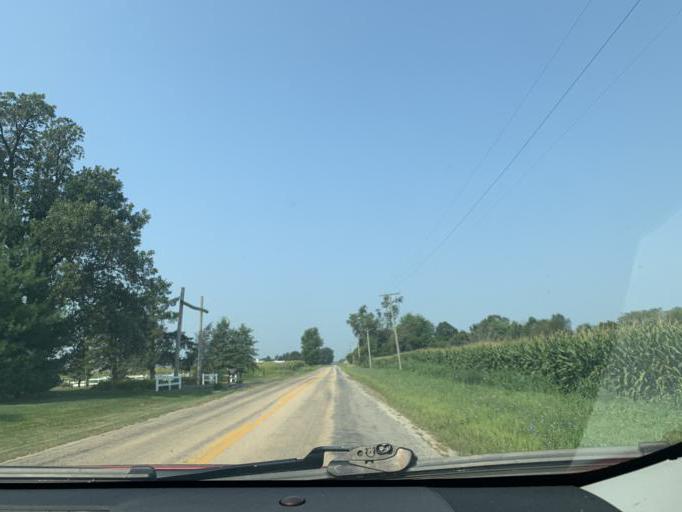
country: US
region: Illinois
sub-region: Whiteside County
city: Morrison
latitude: 41.8480
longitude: -89.8531
